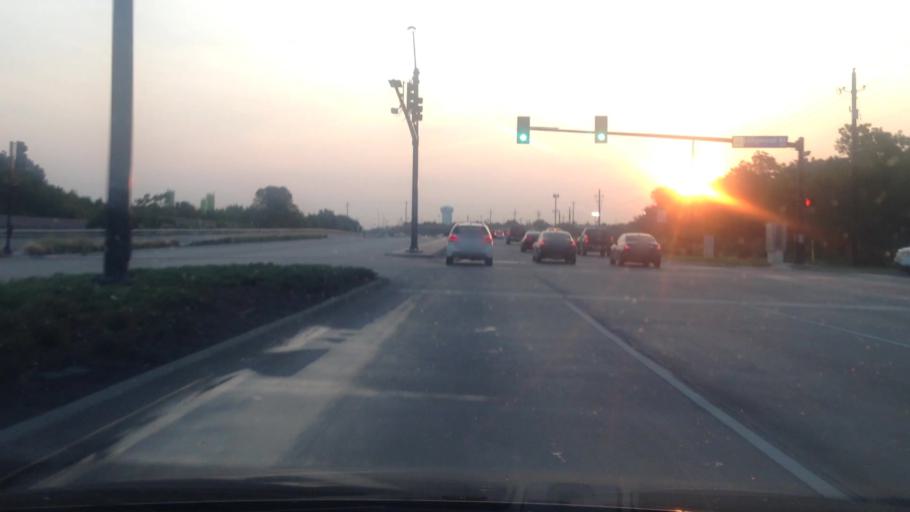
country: US
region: Texas
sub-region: Tarrant County
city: Southlake
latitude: 32.9130
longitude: -97.1310
